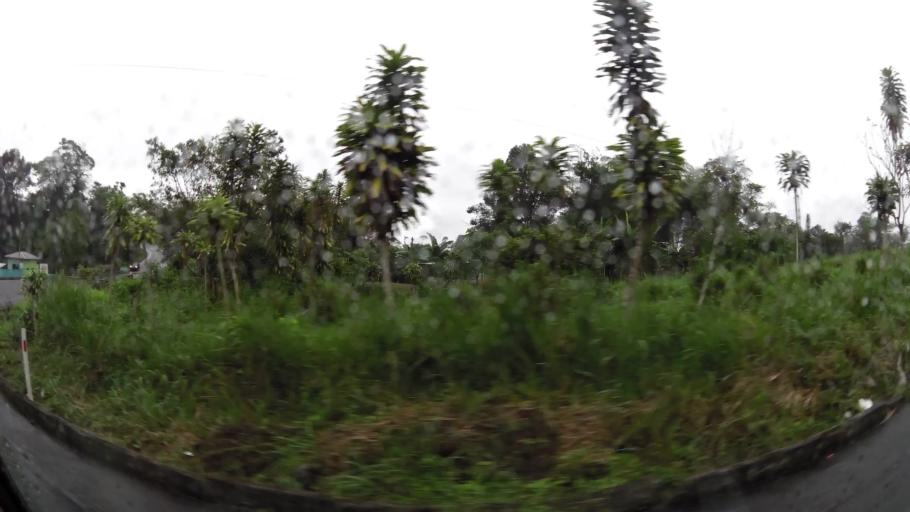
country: EC
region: Santo Domingo de los Tsachilas
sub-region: Canton Santo Domingo de los Colorados
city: Santo Domingo de los Colorados
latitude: -0.2238
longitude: -79.1225
